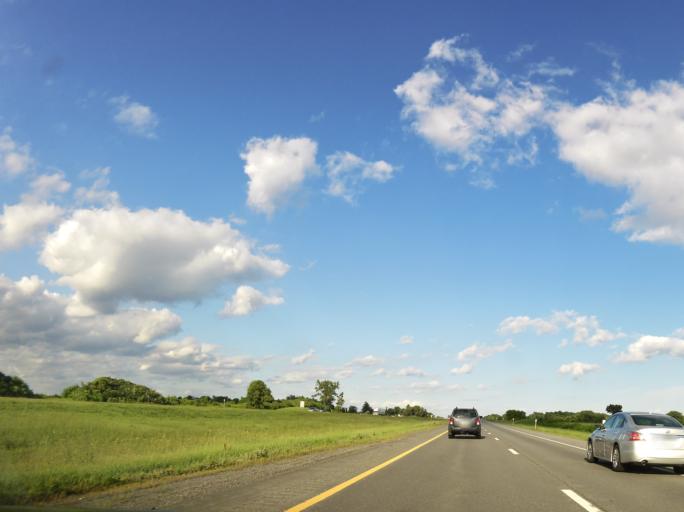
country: US
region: New York
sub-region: Genesee County
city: Batavia
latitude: 43.0172
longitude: -78.2296
